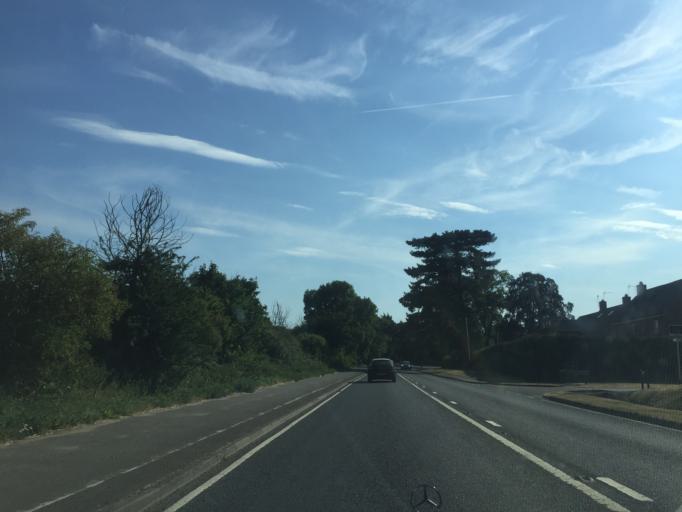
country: GB
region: England
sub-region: Warwickshire
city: Warwick
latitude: 52.2623
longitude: -1.6048
